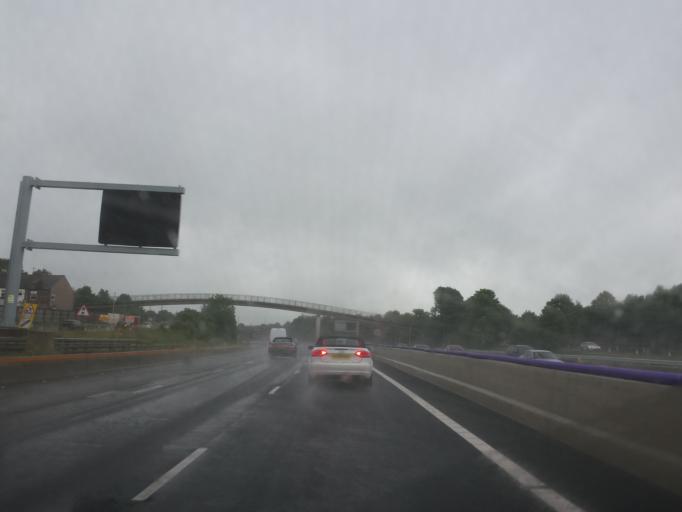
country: GB
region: England
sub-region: Derbyshire
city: Blackwell
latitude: 53.1051
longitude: -1.3270
